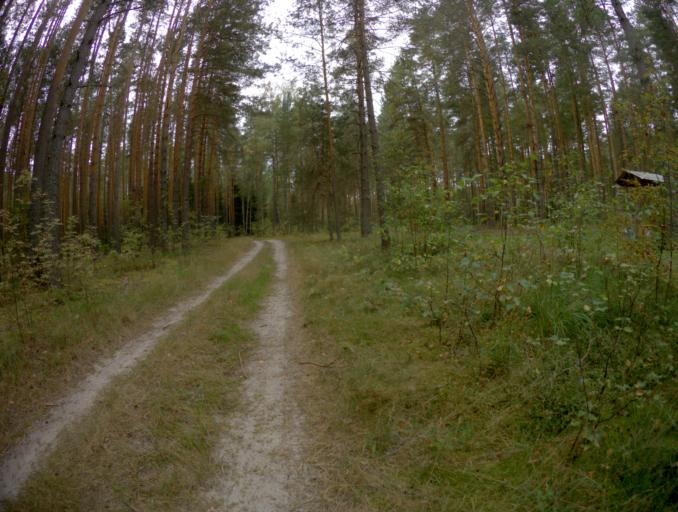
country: RU
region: Vladimir
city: Ivanishchi
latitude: 55.8482
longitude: 40.3484
